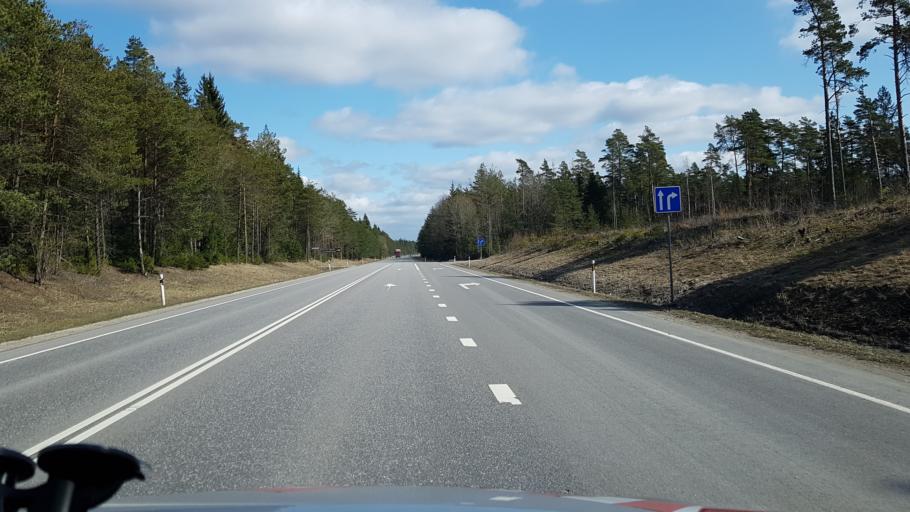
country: EE
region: Laeaene
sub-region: Lihula vald
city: Lihula
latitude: 58.9734
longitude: 23.9128
